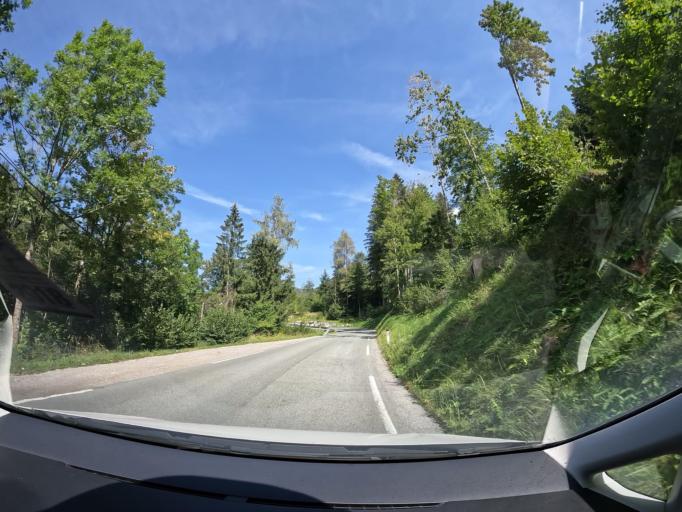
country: AT
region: Carinthia
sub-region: Politischer Bezirk Villach Land
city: Sankt Jakob
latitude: 46.5664
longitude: 14.0736
